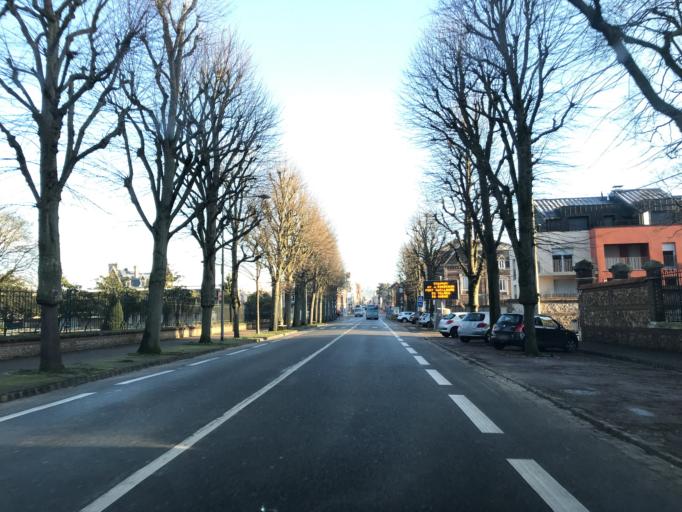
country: FR
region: Haute-Normandie
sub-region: Departement de la Seine-Maritime
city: Sotteville-les-Rouen
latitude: 49.4207
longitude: 1.0790
